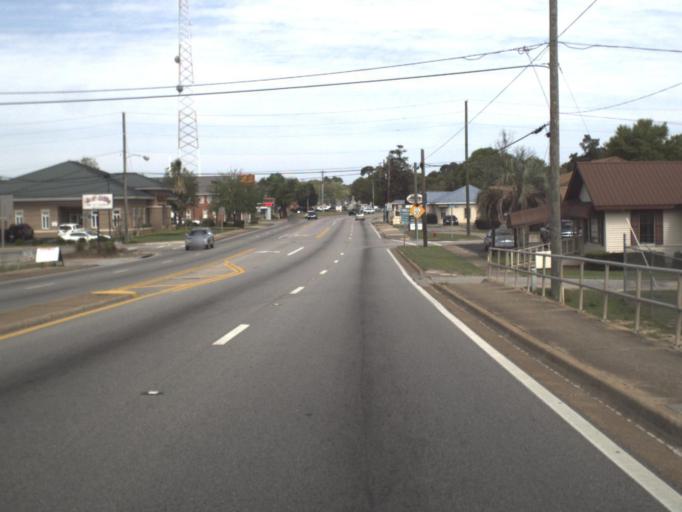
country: US
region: Florida
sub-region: Okaloosa County
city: Crestview
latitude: 30.7594
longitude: -86.5691
